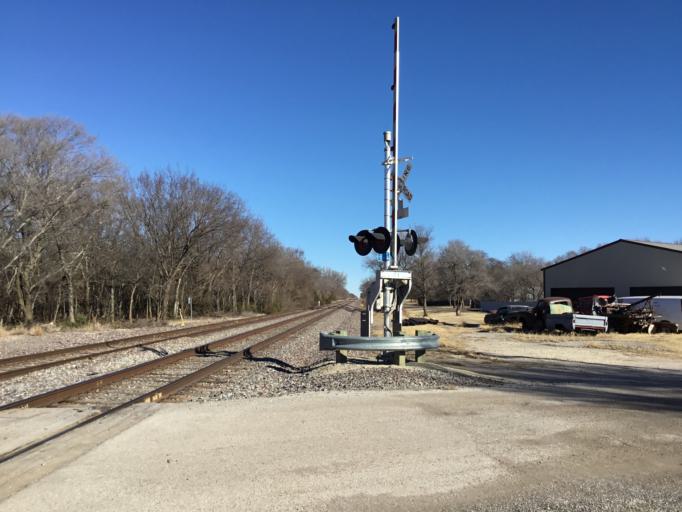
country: US
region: Kansas
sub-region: Marion County
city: Peabody
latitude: 37.9661
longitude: -97.1503
